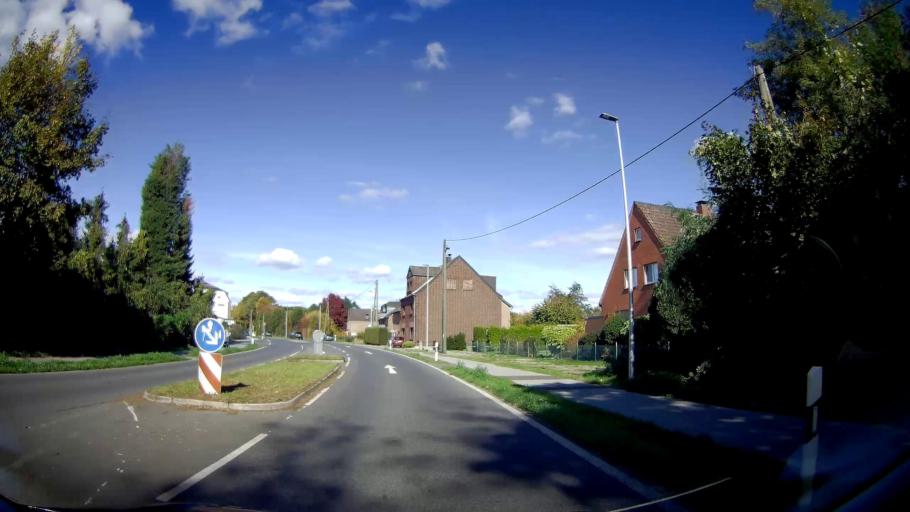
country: DE
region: North Rhine-Westphalia
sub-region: Regierungsbezirk Dusseldorf
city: Dinslaken
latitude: 51.5997
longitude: 6.7580
